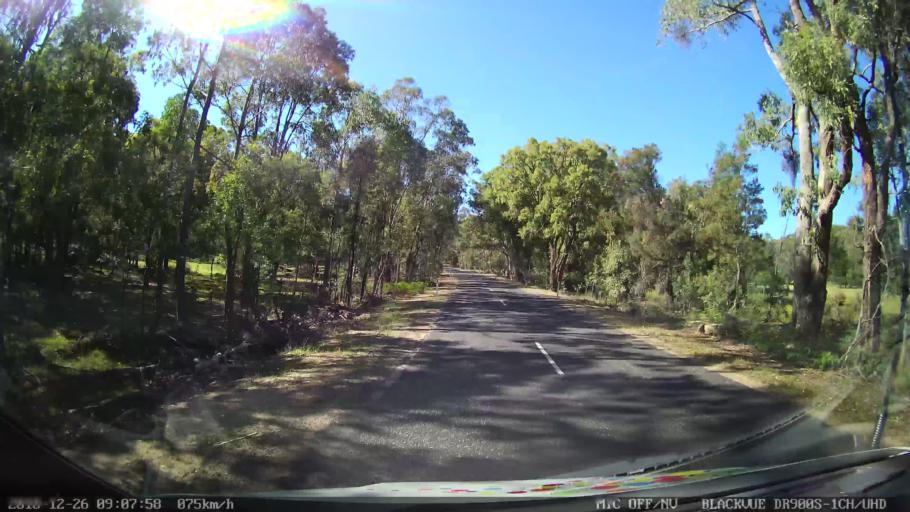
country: AU
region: New South Wales
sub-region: Mid-Western Regional
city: Kandos
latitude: -32.7114
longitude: 150.0030
